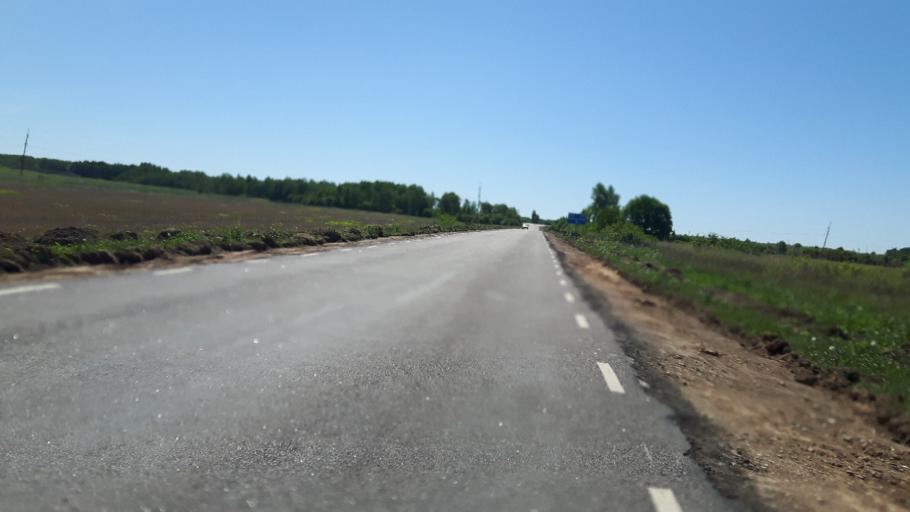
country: EE
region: Ida-Virumaa
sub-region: Narva-Joesuu linn
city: Narva-Joesuu
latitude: 59.3837
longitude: 27.9209
